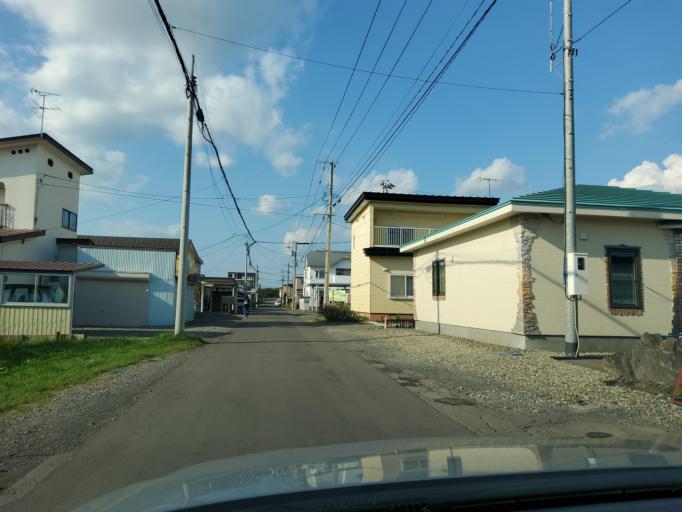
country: JP
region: Hokkaido
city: Obihiro
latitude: 42.8930
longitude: 143.1979
